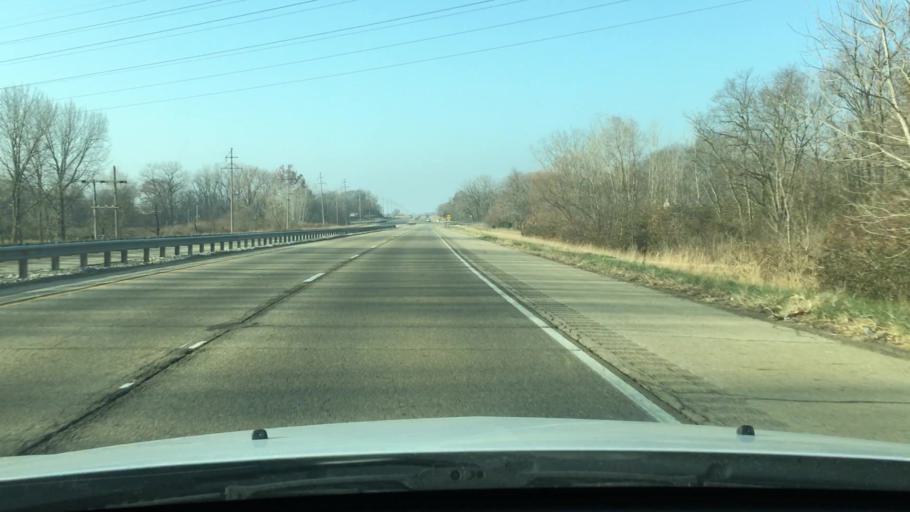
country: US
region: Illinois
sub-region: Tazewell County
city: Pekin
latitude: 40.5833
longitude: -89.6895
